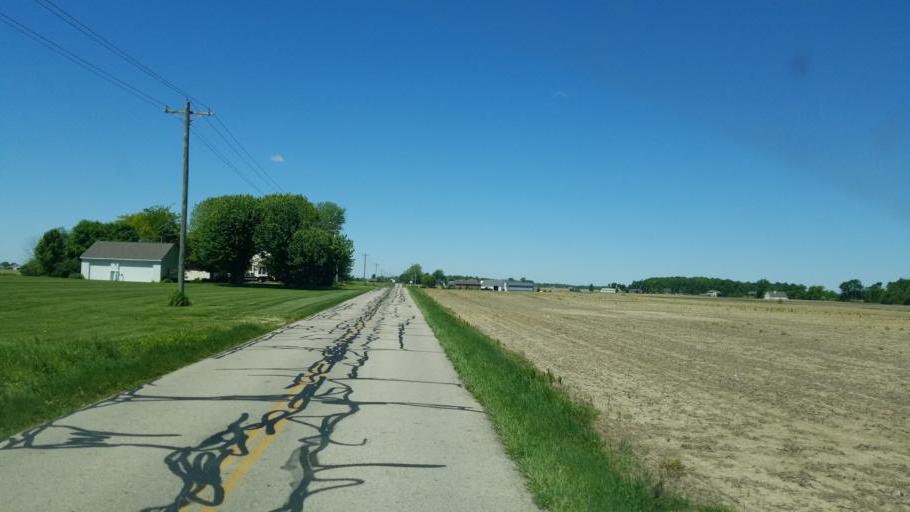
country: US
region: Ohio
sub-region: Shelby County
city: Anna
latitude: 40.3803
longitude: -84.2281
